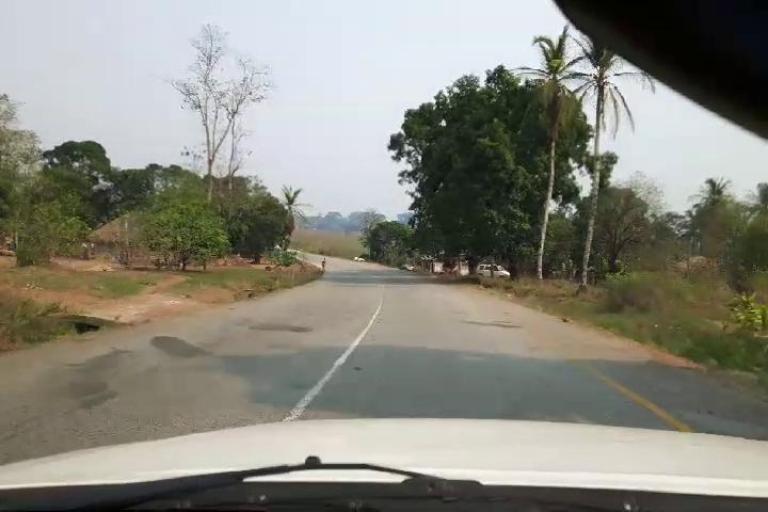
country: SL
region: Southern Province
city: Largo
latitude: 8.2108
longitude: -12.0701
